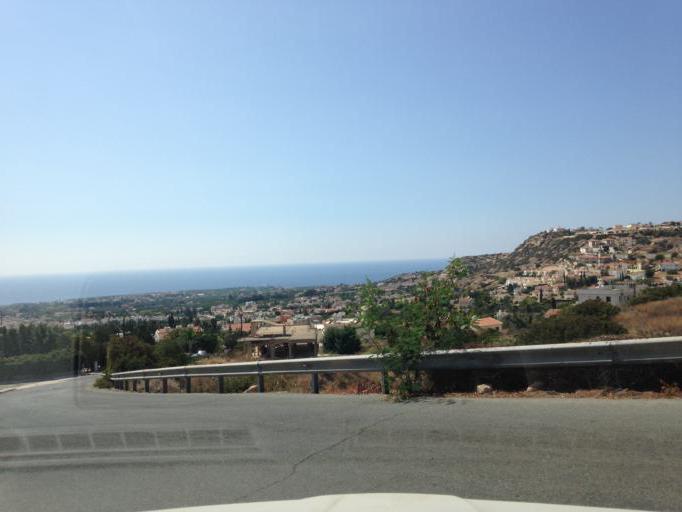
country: CY
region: Pafos
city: Pegeia
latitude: 34.8836
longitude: 32.3752
